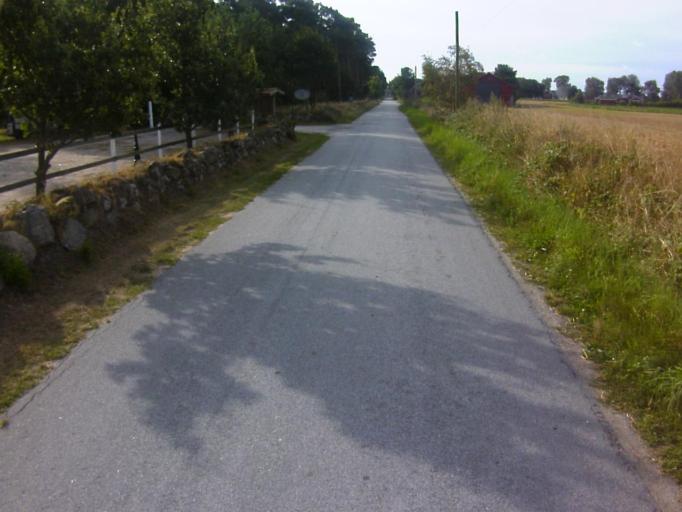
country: SE
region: Blekinge
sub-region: Solvesborgs Kommun
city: Soelvesborg
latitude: 56.0297
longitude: 14.7108
